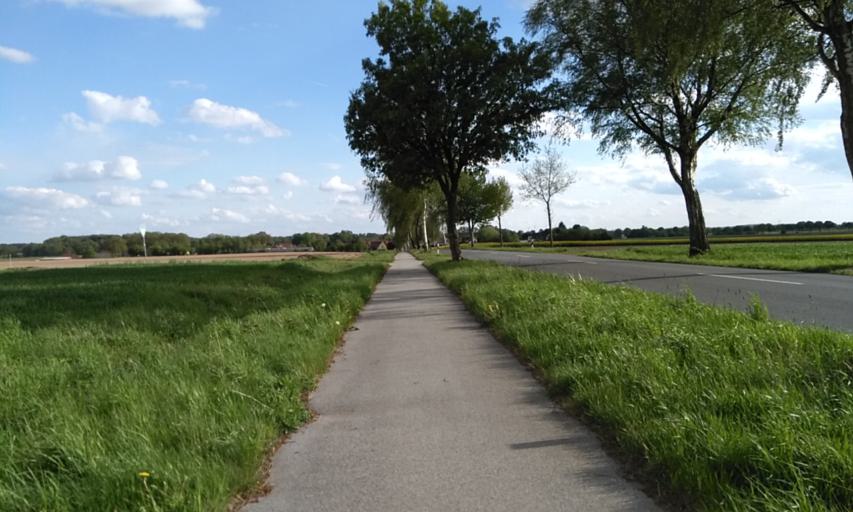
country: DE
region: Lower Saxony
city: Beckdorf
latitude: 53.4239
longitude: 9.6552
